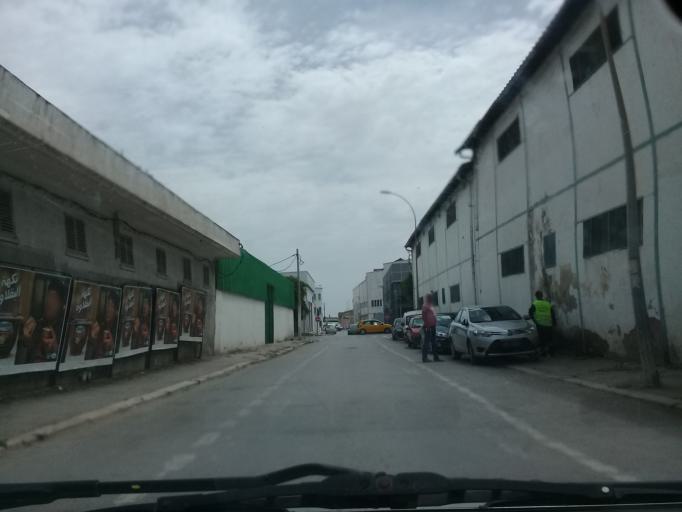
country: TN
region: Tunis
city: Tunis
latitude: 36.7946
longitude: 10.1863
